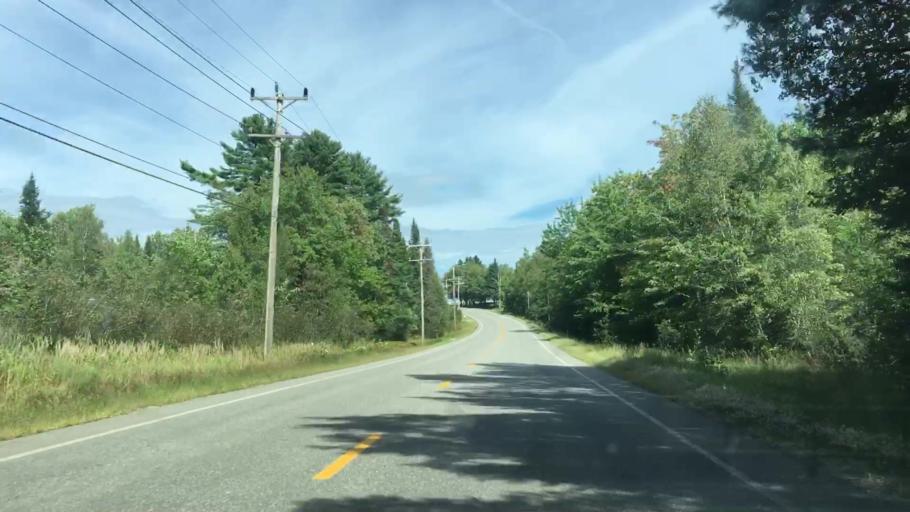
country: US
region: Maine
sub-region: Penobscot County
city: Lincoln
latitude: 45.3948
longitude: -68.5149
